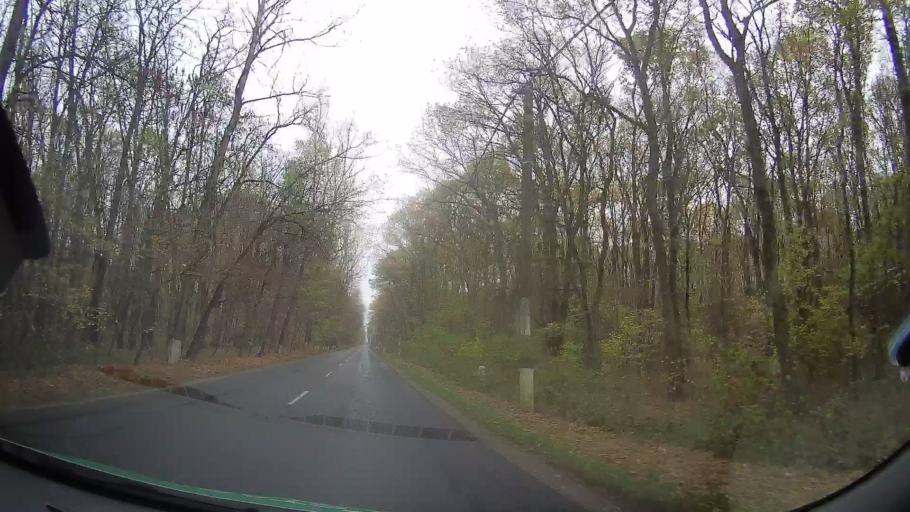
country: RO
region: Ilfov
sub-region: Comuna Snagov
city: Snagov
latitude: 44.7149
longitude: 26.1952
